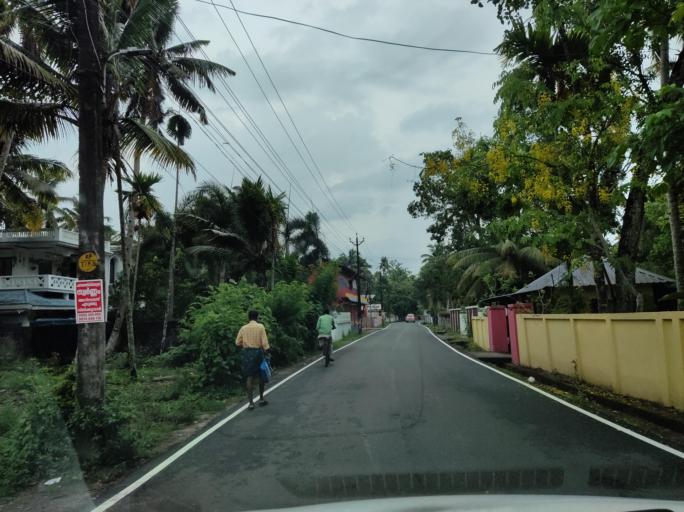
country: IN
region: Kerala
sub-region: Alappuzha
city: Kayankulam
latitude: 9.2644
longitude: 76.4086
